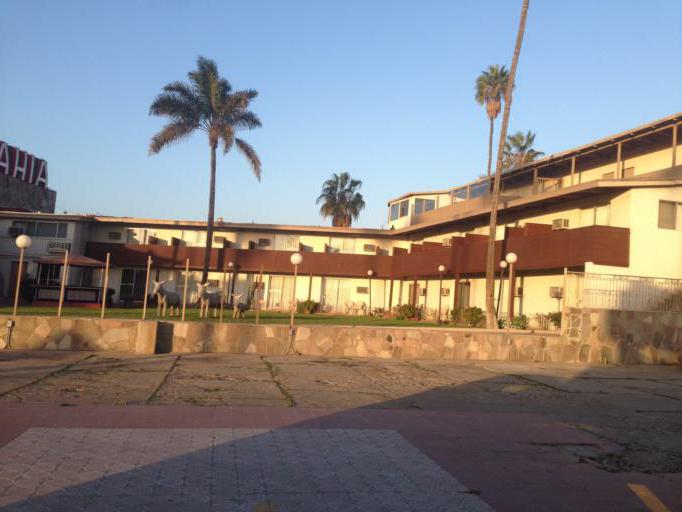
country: MX
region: Baja California
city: Ensenada
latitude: 31.8610
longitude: -116.6238
